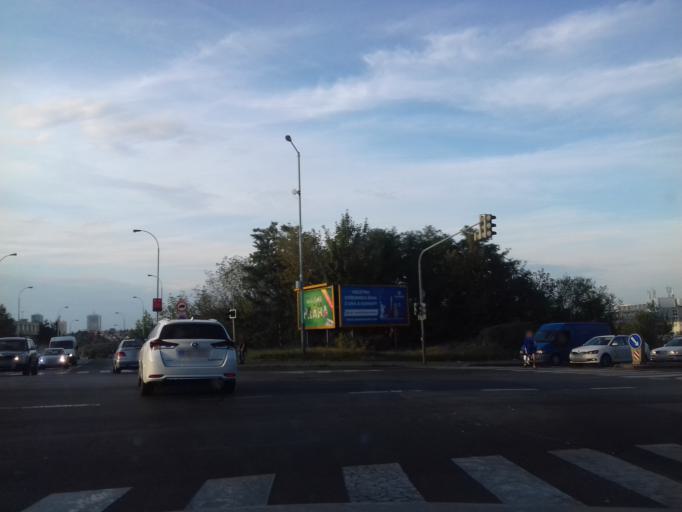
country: CZ
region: Praha
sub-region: Praha 4
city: Hodkovicky
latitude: 50.0279
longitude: 14.4513
